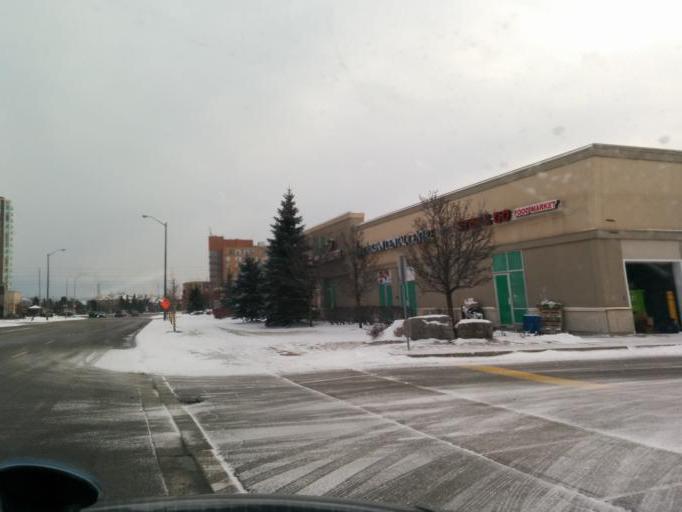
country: CA
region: Ontario
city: Mississauga
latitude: 43.5528
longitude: -79.7166
